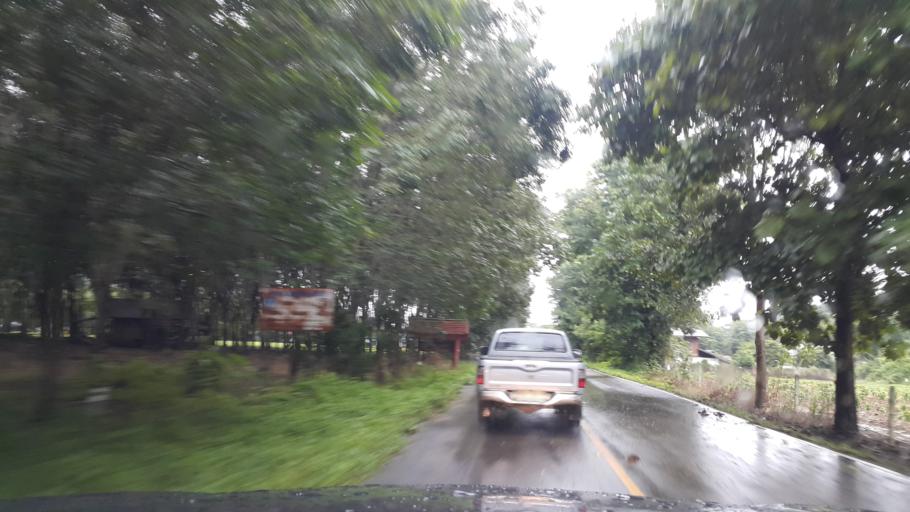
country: TH
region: Phayao
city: Phu Sang
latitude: 19.6064
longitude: 100.4066
